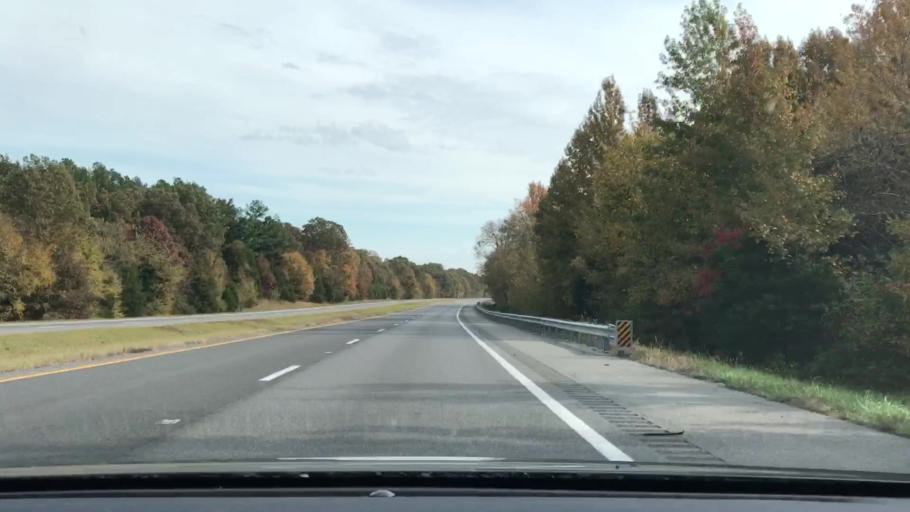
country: US
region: Kentucky
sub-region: Graves County
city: Mayfield
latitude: 36.7864
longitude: -88.5433
